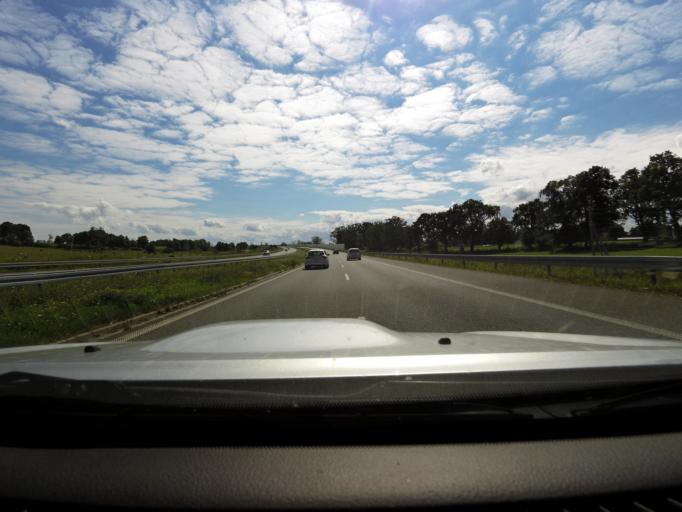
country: PL
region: Warmian-Masurian Voivodeship
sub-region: Powiat ostrodzki
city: Milomlyn
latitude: 53.7865
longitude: 19.7994
